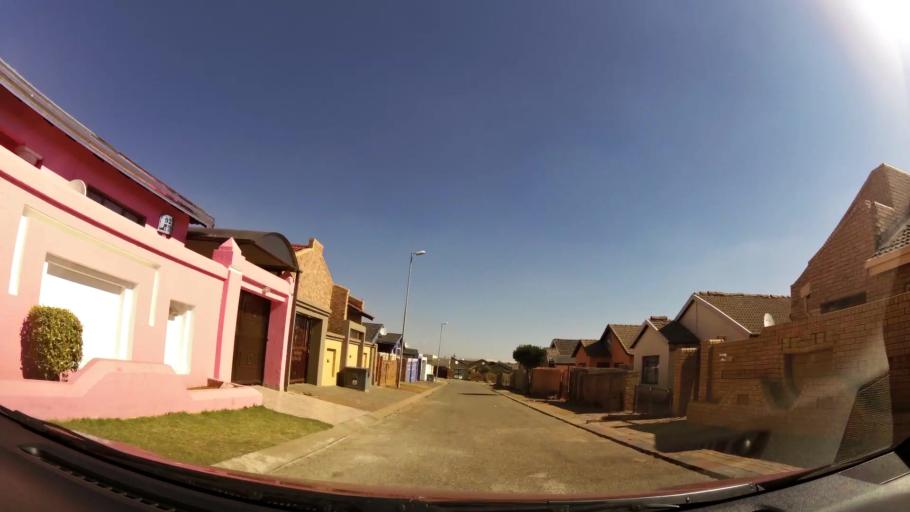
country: ZA
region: Gauteng
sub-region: City of Johannesburg Metropolitan Municipality
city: Soweto
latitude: -26.2353
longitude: 27.8230
